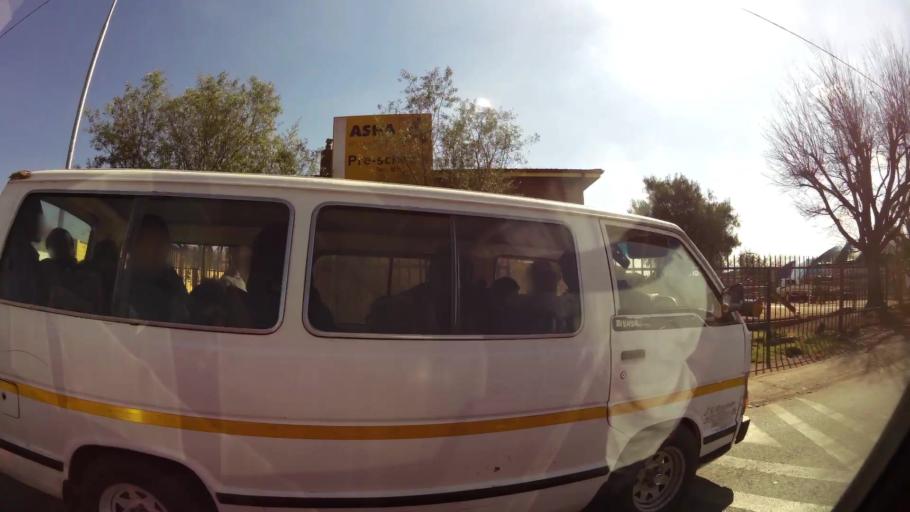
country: ZA
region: Gauteng
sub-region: City of Johannesburg Metropolitan Municipality
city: Soweto
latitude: -26.2289
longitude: 27.8840
